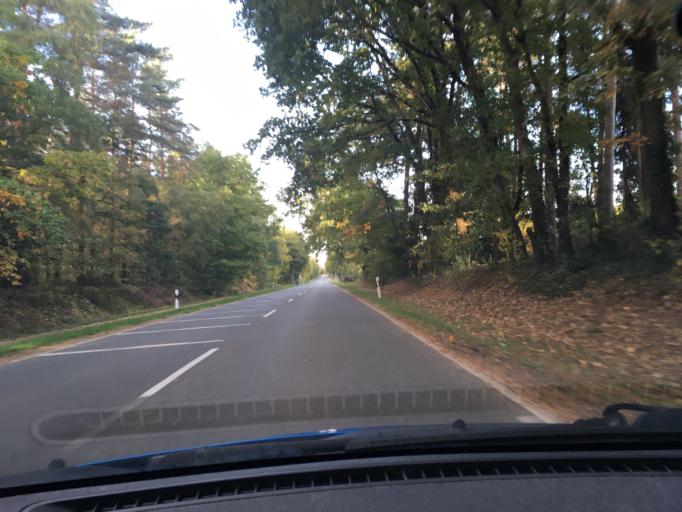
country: DE
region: Lower Saxony
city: Fassberg
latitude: 52.9344
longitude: 10.1343
